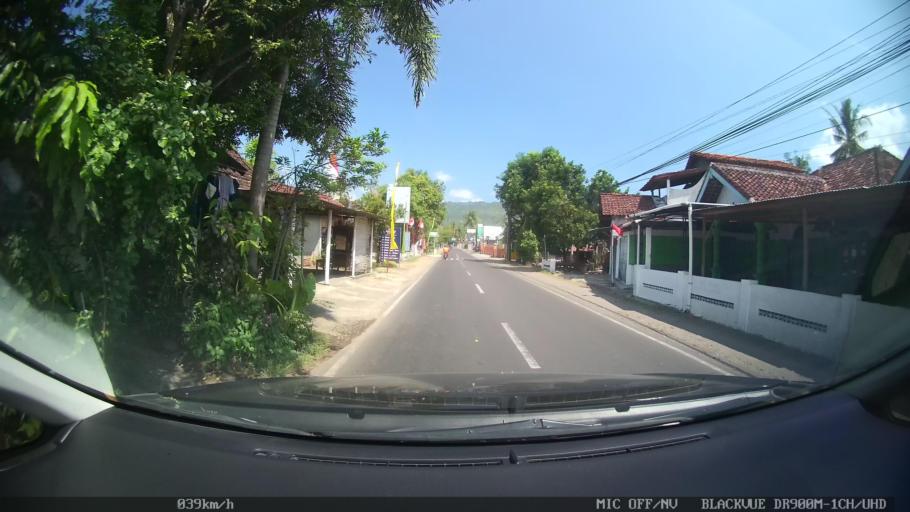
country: ID
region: Daerah Istimewa Yogyakarta
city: Pundong
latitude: -7.9437
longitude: 110.3743
